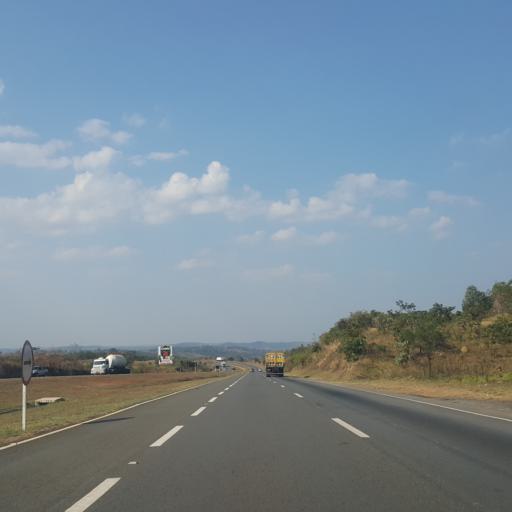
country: BR
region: Goias
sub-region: Abadiania
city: Abadiania
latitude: -16.1857
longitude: -48.6600
